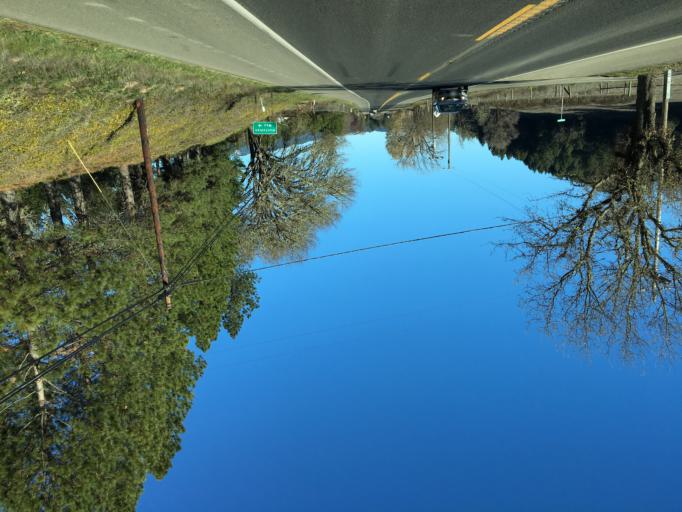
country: US
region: California
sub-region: Mendocino County
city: Laytonville
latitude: 39.7022
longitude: -123.4870
